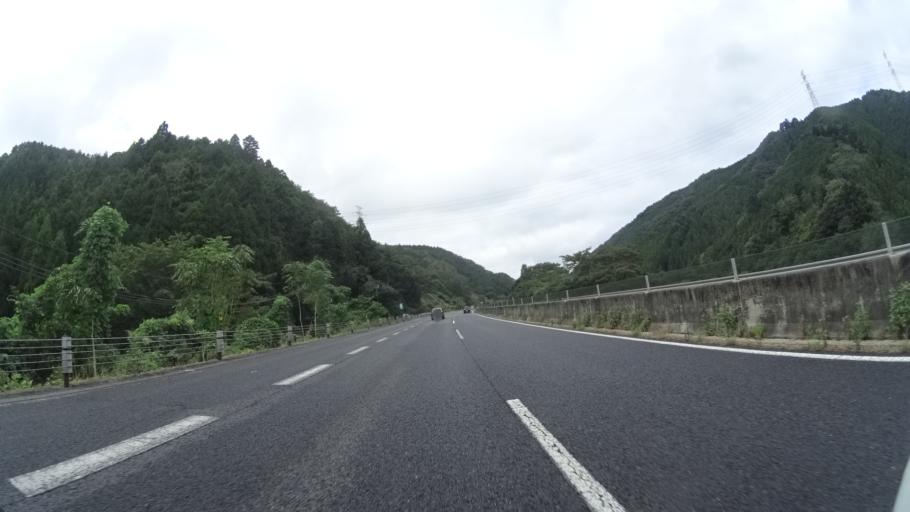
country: JP
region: Hyogo
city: Yamazakicho-nakabirose
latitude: 35.0371
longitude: 134.4750
